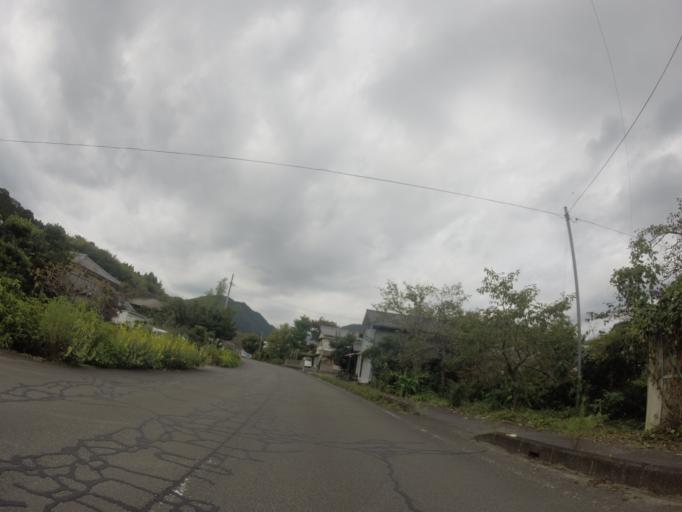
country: JP
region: Shizuoka
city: Fujieda
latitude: 34.9090
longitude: 138.1938
